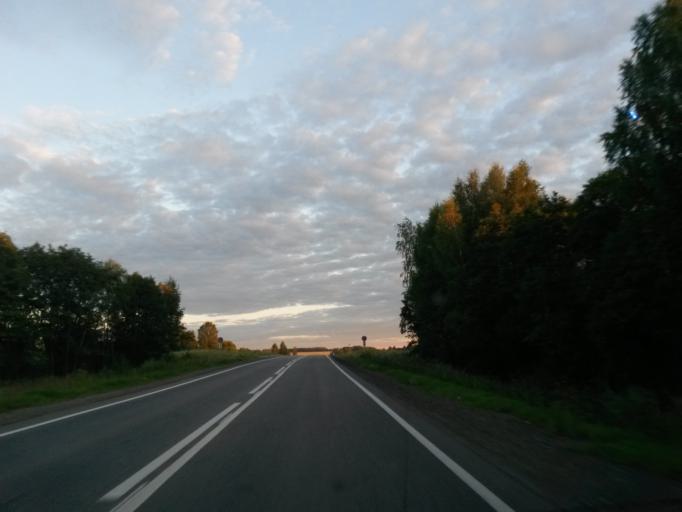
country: RU
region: Jaroslavl
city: Gavrilov-Yam
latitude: 57.3343
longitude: 39.9206
